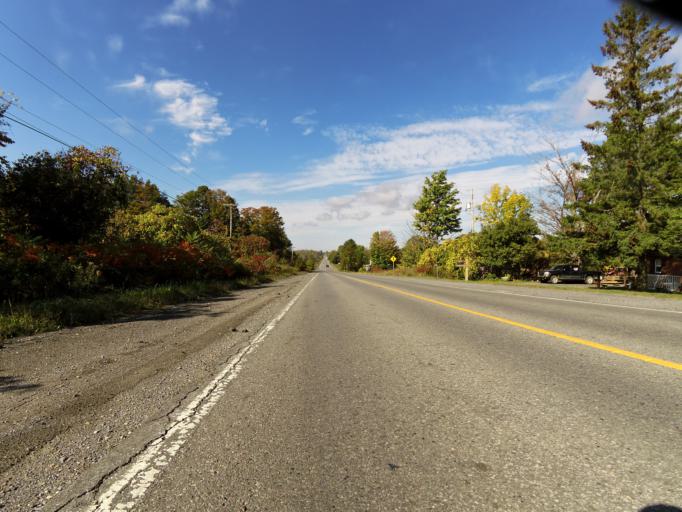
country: CA
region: Ontario
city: Prince Edward
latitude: 43.9976
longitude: -77.1937
